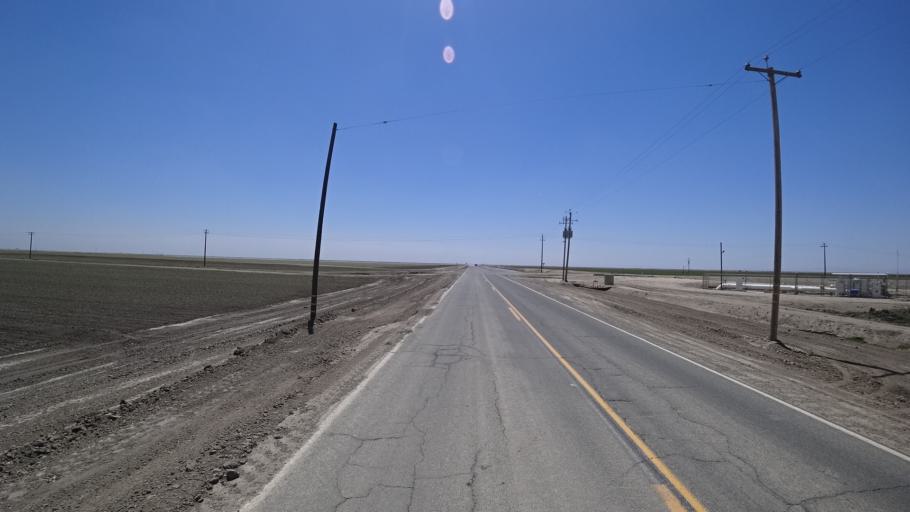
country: US
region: California
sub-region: Kings County
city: Corcoran
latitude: 36.0805
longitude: -119.6440
